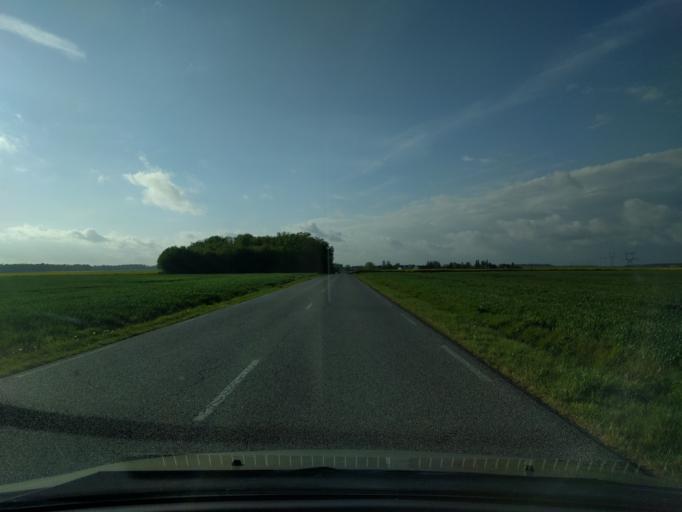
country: FR
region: Haute-Normandie
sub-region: Departement de l'Eure
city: Damville
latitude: 48.9015
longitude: 1.0302
